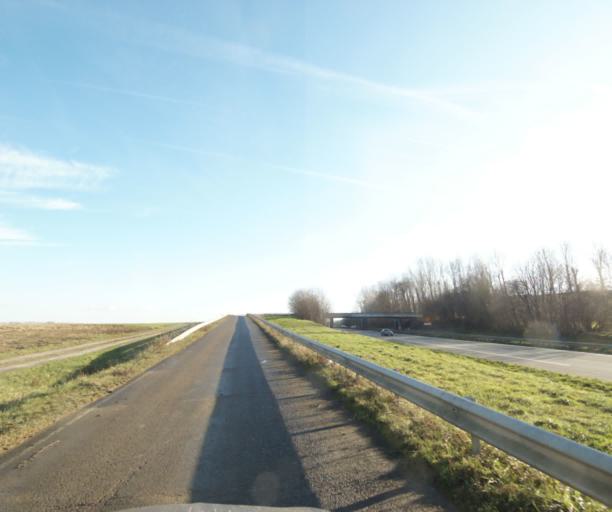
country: FR
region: Nord-Pas-de-Calais
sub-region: Departement du Nord
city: Curgies
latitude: 50.3213
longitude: 3.6025
